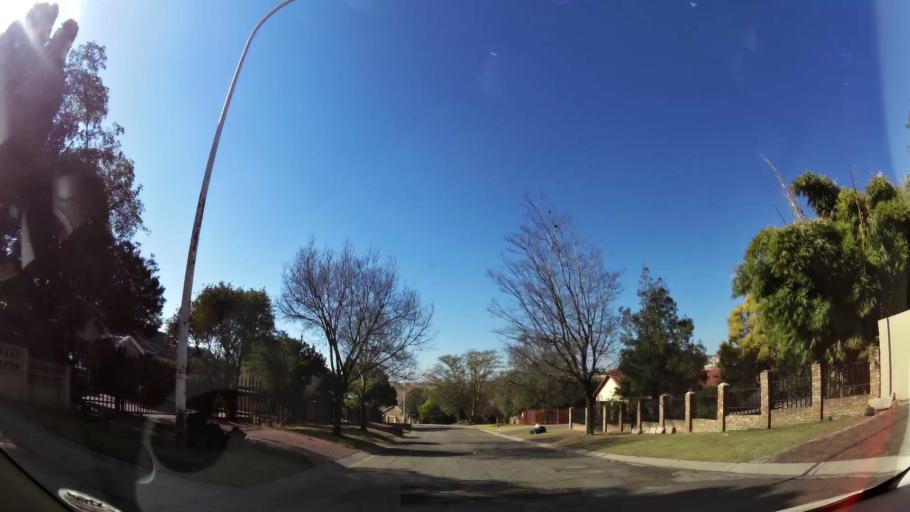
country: ZA
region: Mpumalanga
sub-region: Nkangala District Municipality
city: Witbank
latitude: -25.8763
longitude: 29.2493
